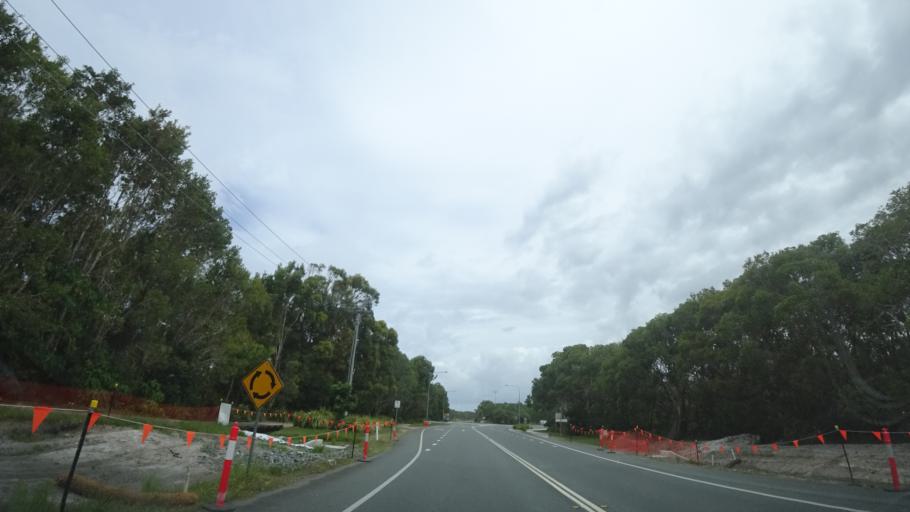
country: AU
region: Queensland
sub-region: Sunshine Coast
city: Coolum Beach
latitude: -26.5676
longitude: 153.0927
